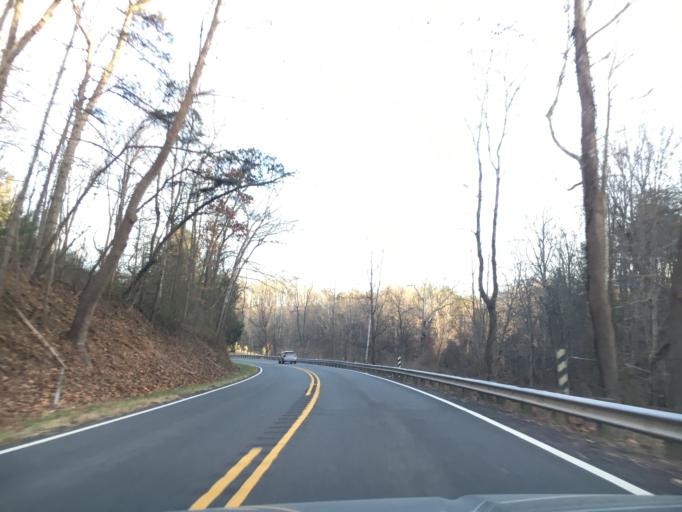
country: US
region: Virginia
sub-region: Culpeper County
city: Merrimac
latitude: 38.5551
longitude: -78.1537
